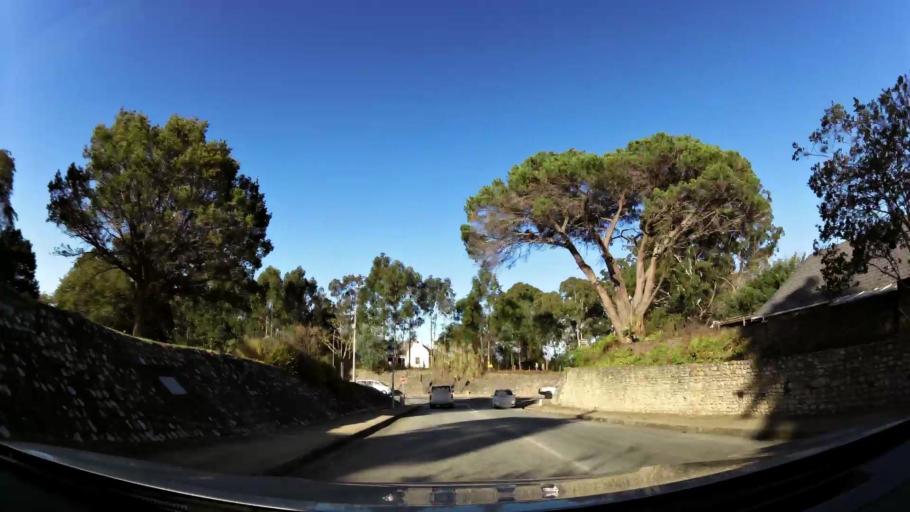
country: ZA
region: Western Cape
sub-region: Eden District Municipality
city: George
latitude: -33.9519
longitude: 22.4541
